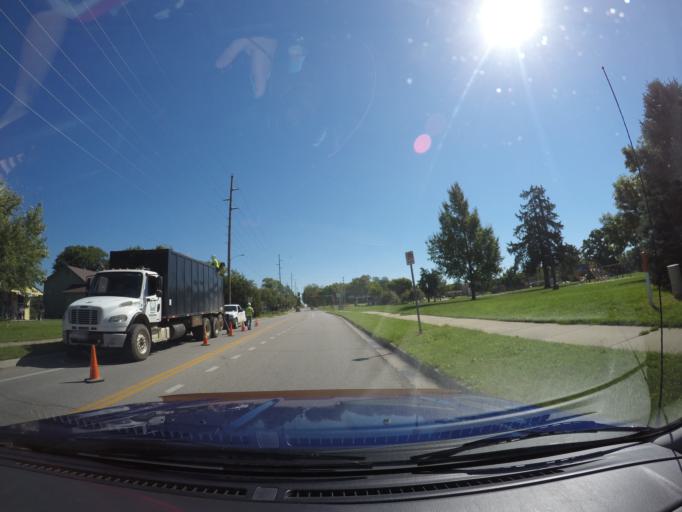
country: US
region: Kansas
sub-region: Douglas County
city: Lawrence
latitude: 38.9499
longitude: -95.2247
